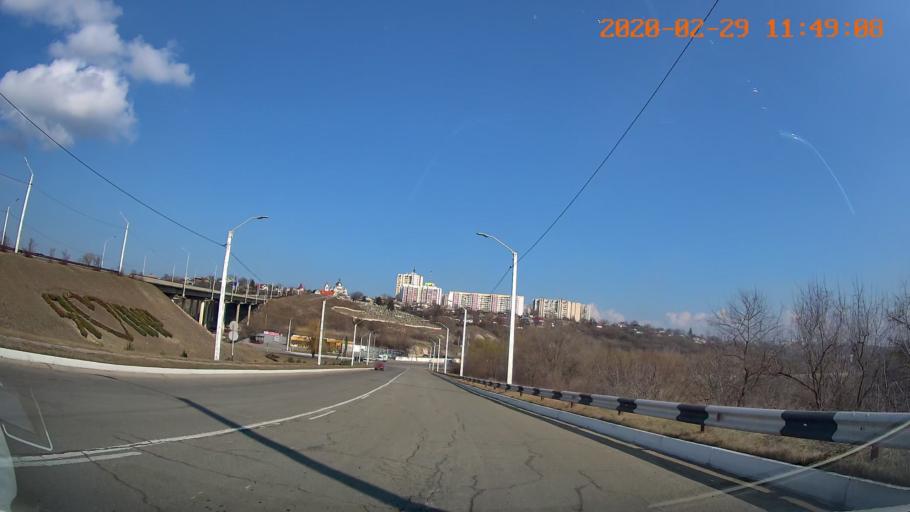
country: MD
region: Telenesti
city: Ribnita
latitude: 47.7530
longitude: 28.9947
